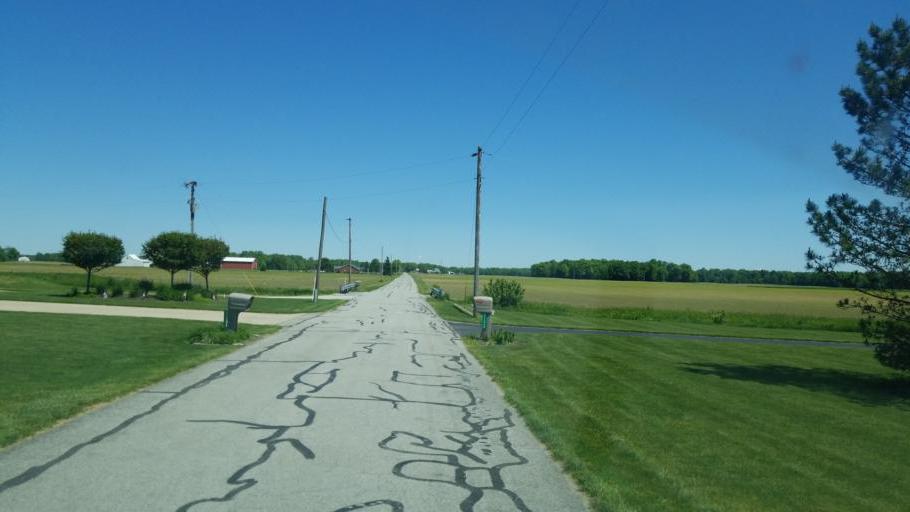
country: US
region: Ohio
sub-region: Shelby County
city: Fort Loramie
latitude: 40.3601
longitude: -84.3166
